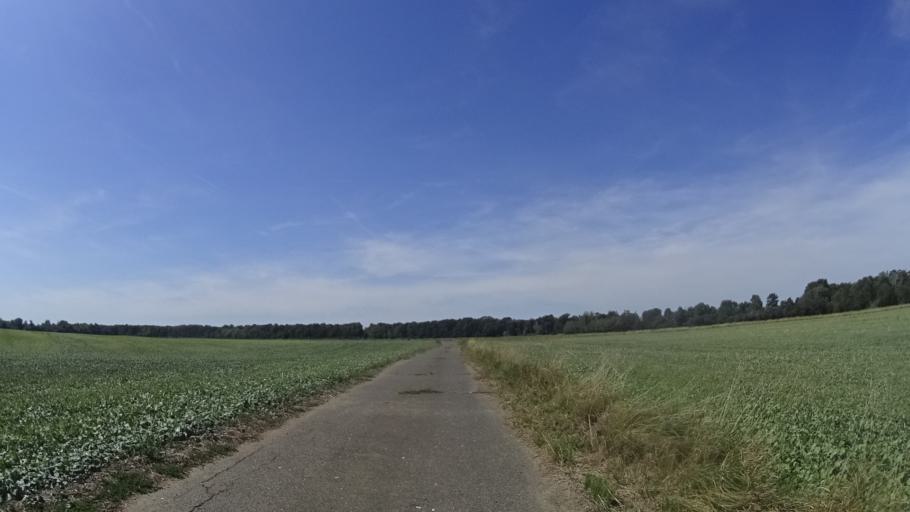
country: AT
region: Lower Austria
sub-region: Politischer Bezirk Ganserndorf
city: Angern an der March
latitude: 48.3660
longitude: 16.8665
